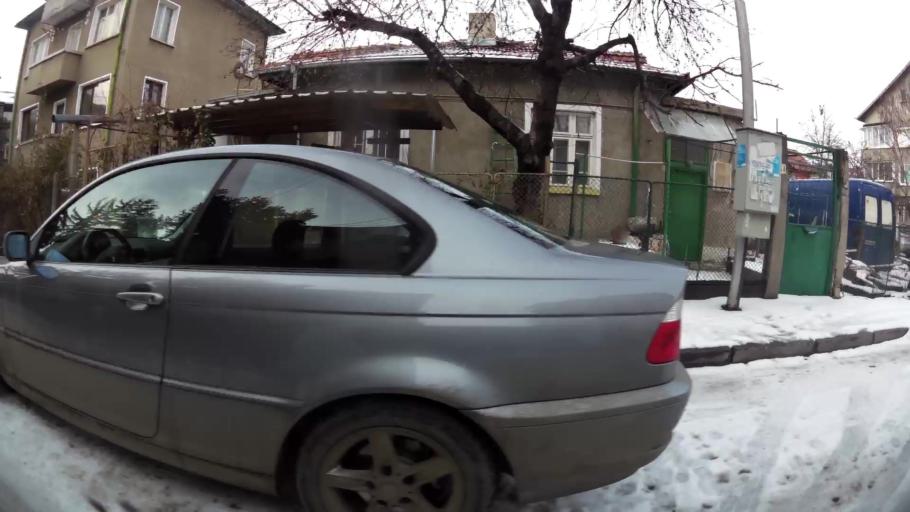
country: BG
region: Sofia-Capital
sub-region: Stolichna Obshtina
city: Sofia
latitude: 42.6981
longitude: 23.3698
